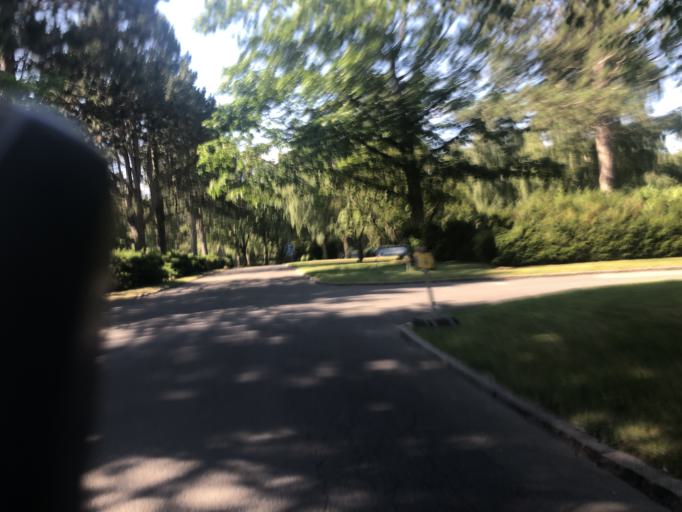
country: DK
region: Capital Region
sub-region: Gladsaxe Municipality
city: Buddinge
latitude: 55.7378
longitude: 12.4680
